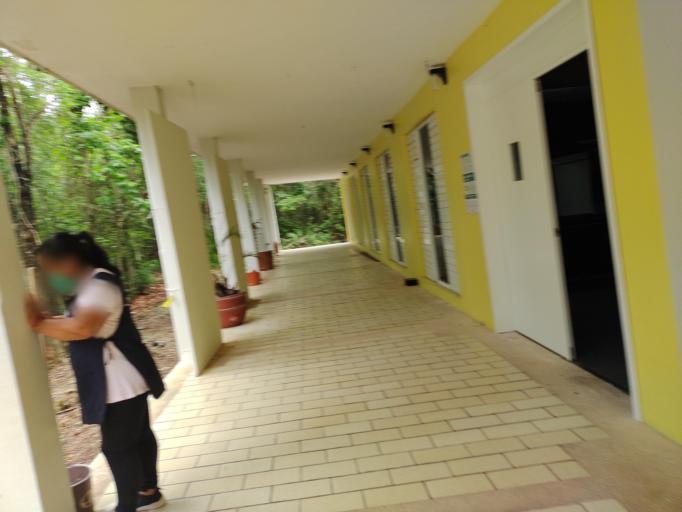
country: MX
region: Quintana Roo
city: San Miguel de Cozumel
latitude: 20.4887
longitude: -86.9395
